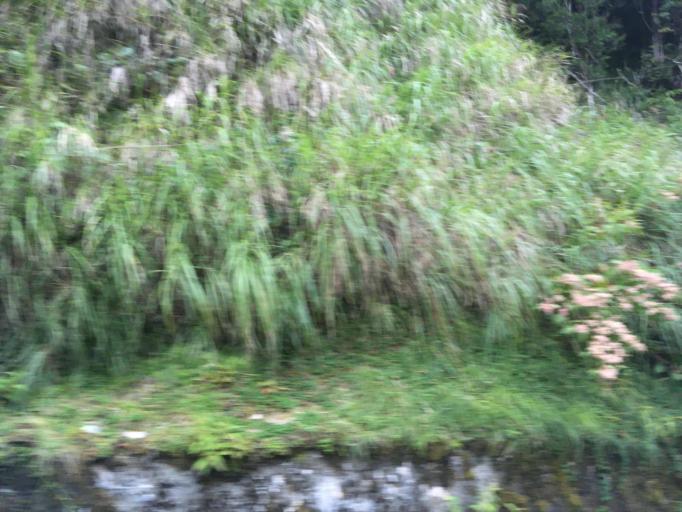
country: TW
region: Taiwan
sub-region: Yilan
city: Yilan
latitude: 24.5141
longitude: 121.5870
